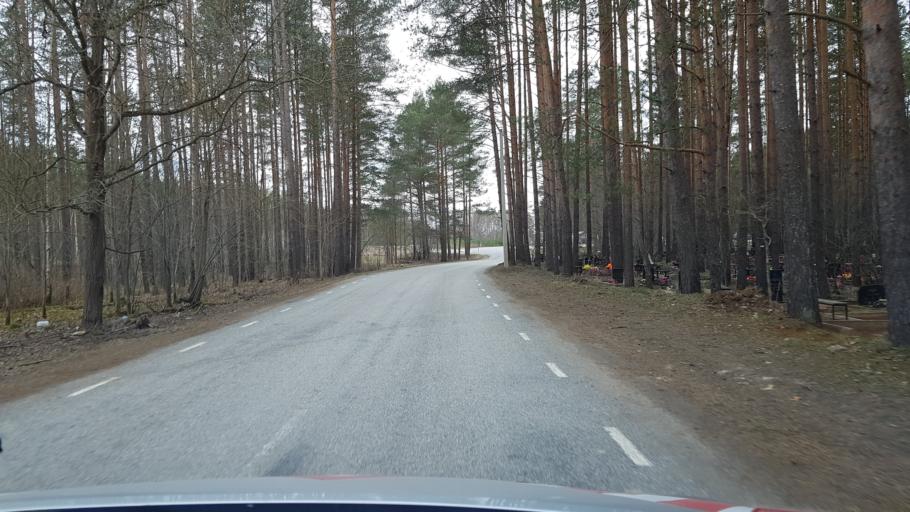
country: EE
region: Ida-Virumaa
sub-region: Narva-Joesuu linn
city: Narva-Joesuu
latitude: 59.4207
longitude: 28.1092
